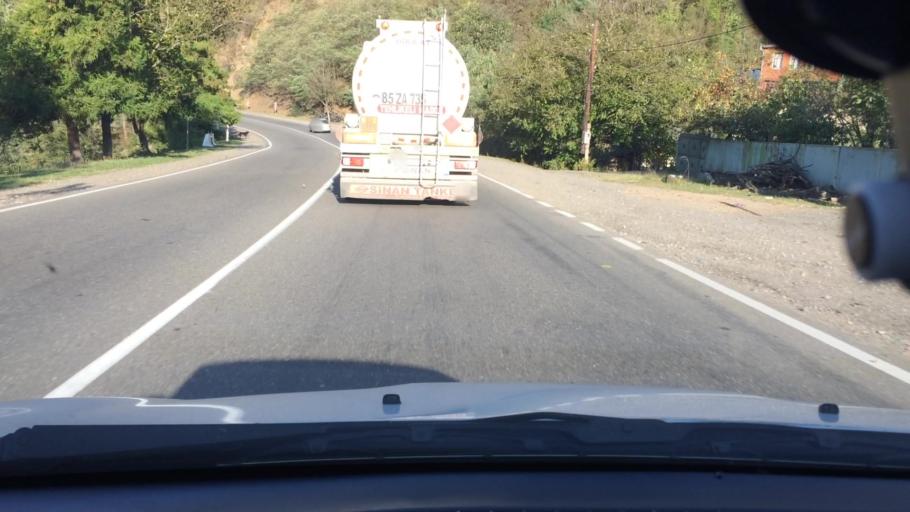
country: GE
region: Imereti
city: Kharagauli
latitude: 42.1107
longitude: 43.1802
